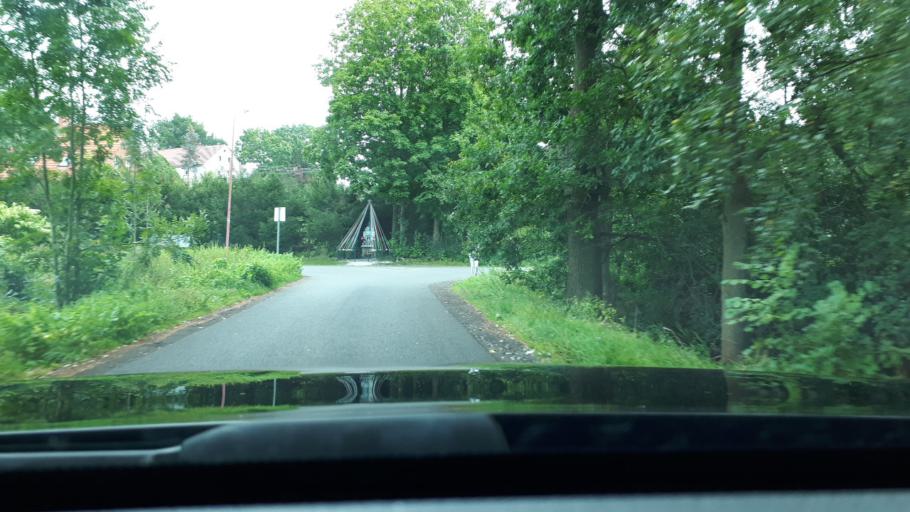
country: PL
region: Lower Silesian Voivodeship
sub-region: Powiat lubanski
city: Lesna
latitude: 51.0365
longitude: 15.3187
